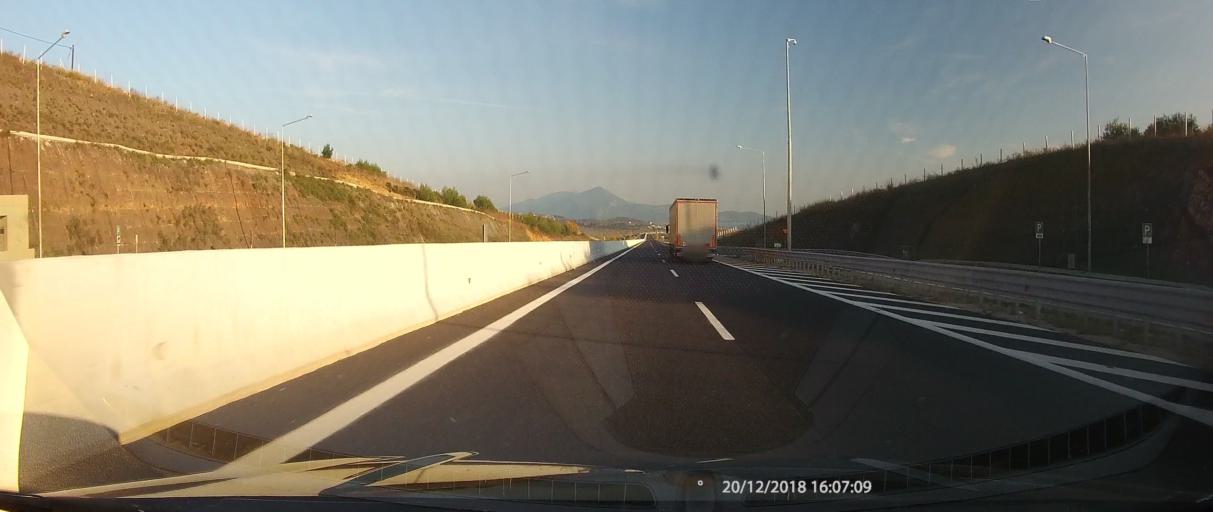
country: GR
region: Central Greece
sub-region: Nomos Fthiotidos
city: Kainouryion
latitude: 38.8980
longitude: 22.7320
